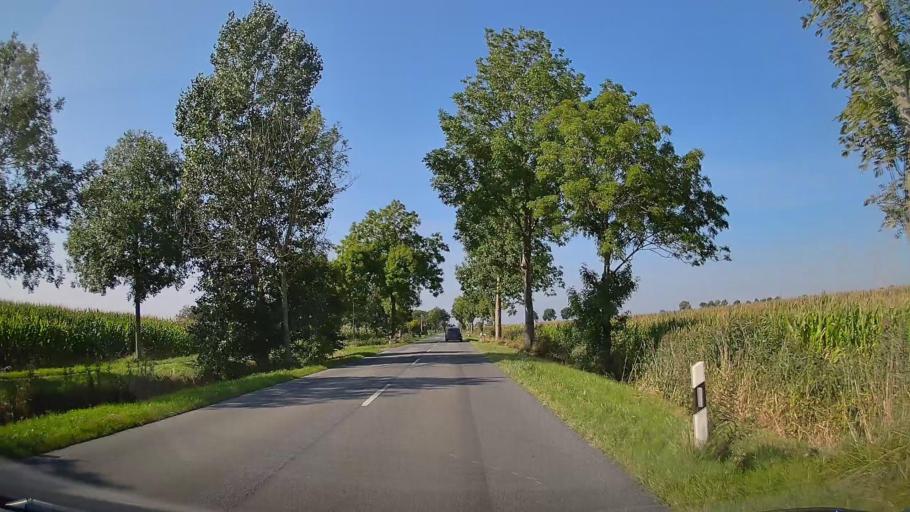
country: DE
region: Lower Saxony
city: Wremen
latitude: 53.6141
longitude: 8.5305
